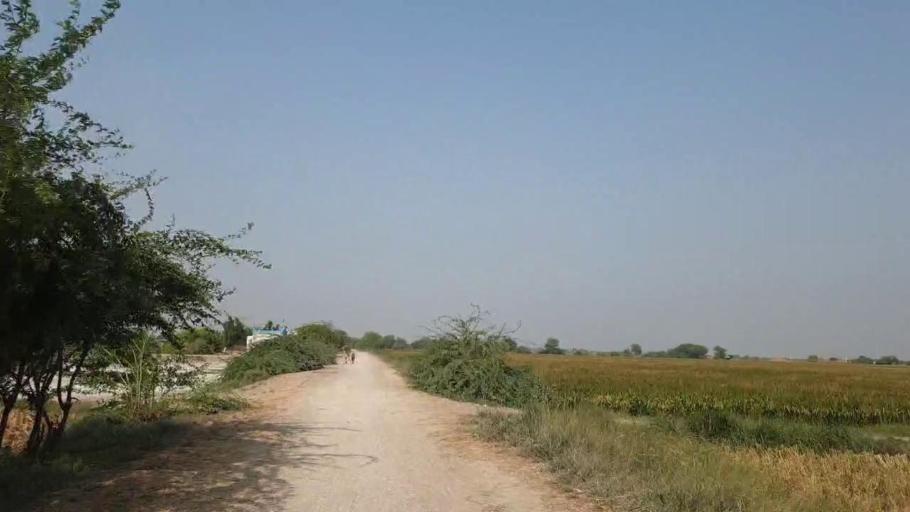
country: PK
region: Sindh
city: Matli
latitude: 24.9466
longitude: 68.5568
